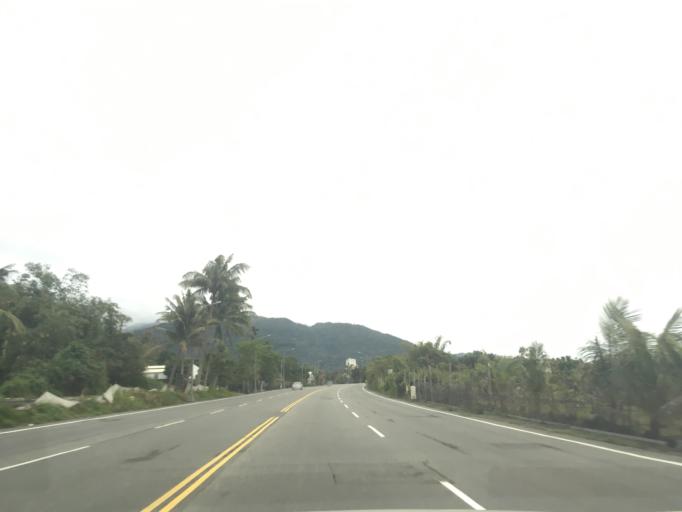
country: TW
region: Taiwan
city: Taitung City
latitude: 22.7436
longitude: 121.0571
